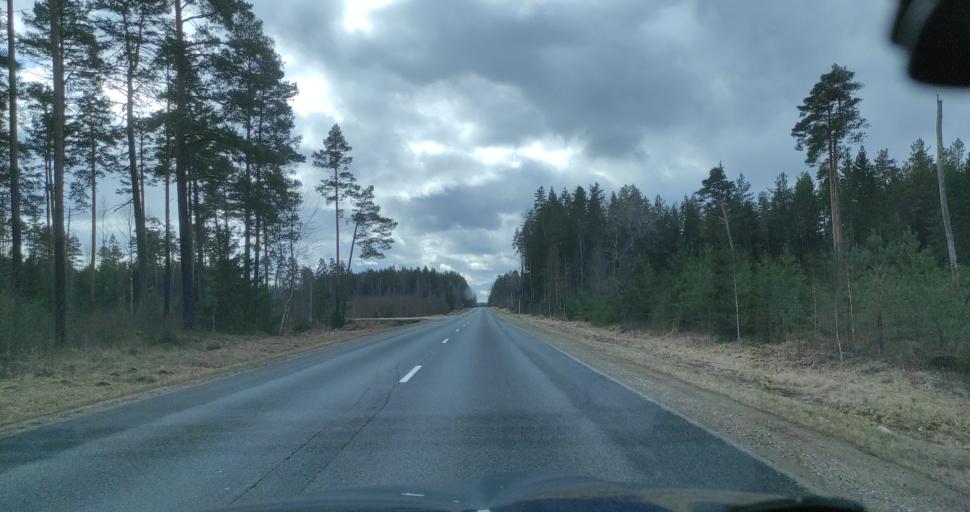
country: LV
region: Talsu Rajons
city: Stende
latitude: 57.0992
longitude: 22.4830
